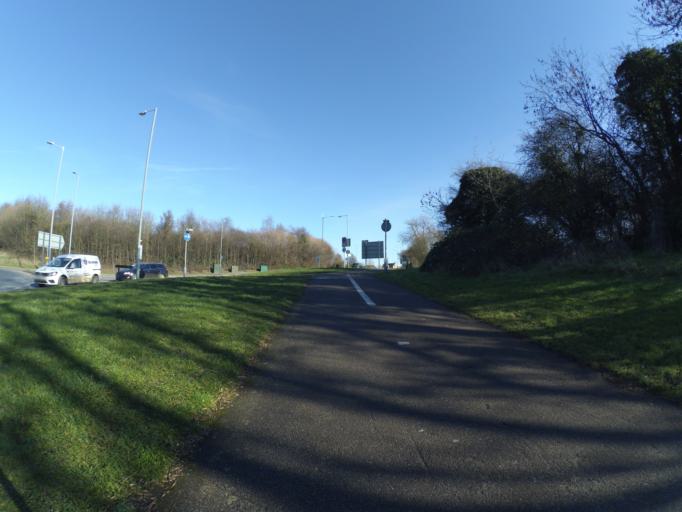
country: GB
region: England
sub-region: Warwickshire
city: Rugby
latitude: 52.3945
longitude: -1.2487
